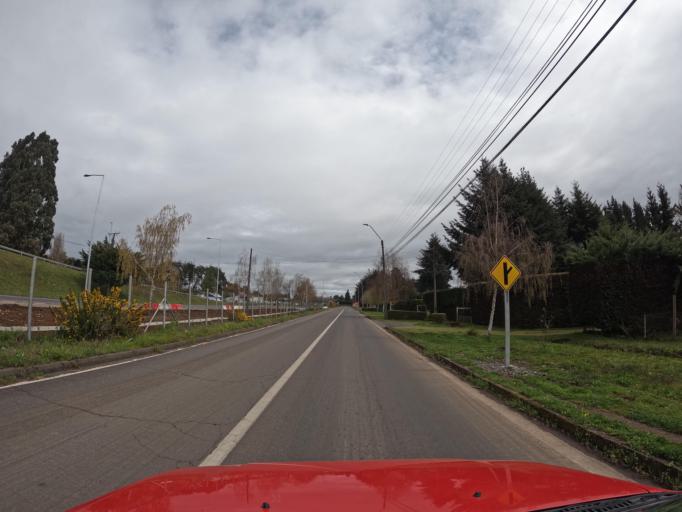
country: CL
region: Araucania
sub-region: Provincia de Malleco
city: Victoria
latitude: -38.2317
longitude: -72.3528
